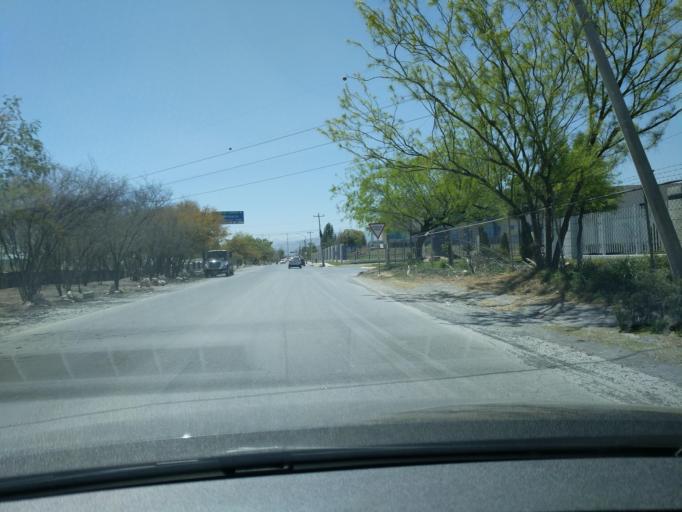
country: MX
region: Nuevo Leon
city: Apodaca
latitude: 25.7911
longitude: -100.1583
